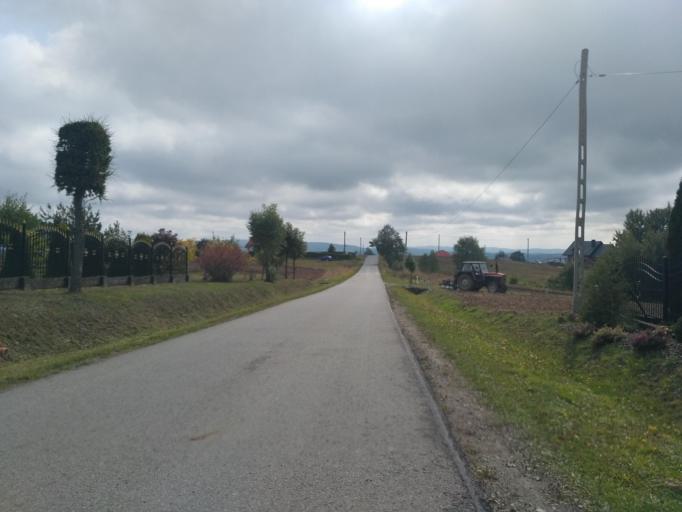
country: PL
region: Subcarpathian Voivodeship
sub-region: Powiat ropczycko-sedziszowski
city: Niedzwiada
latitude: 49.9615
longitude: 21.4510
